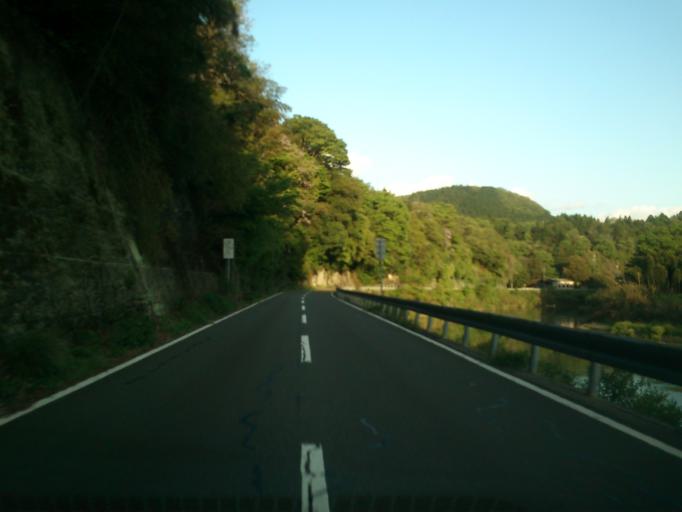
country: JP
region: Kyoto
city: Ayabe
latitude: 35.2765
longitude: 135.3608
